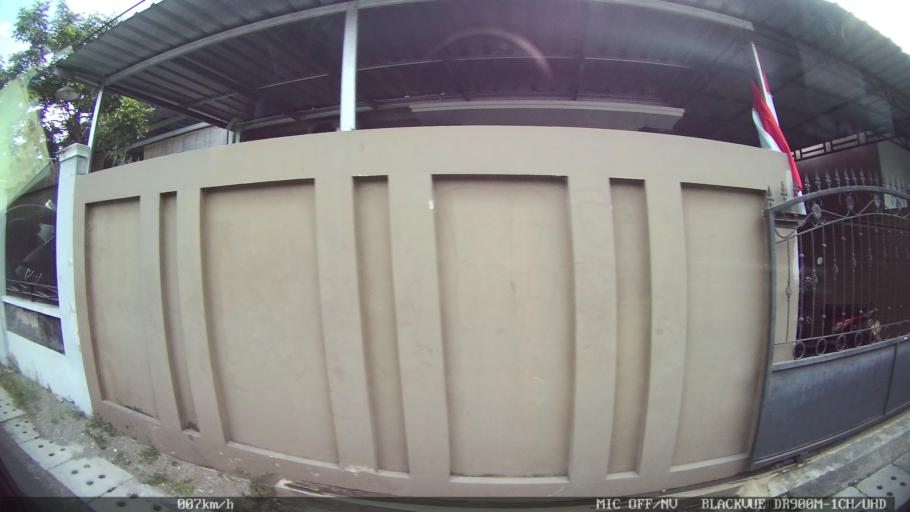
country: ID
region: Daerah Istimewa Yogyakarta
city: Kasihan
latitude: -7.8223
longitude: 110.3325
